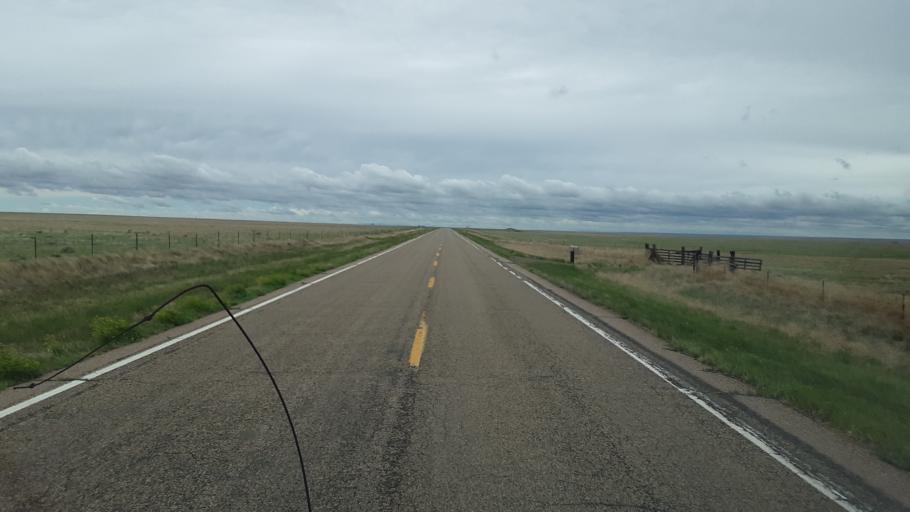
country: US
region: Colorado
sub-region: Lincoln County
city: Hugo
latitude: 38.8521
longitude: -103.7647
